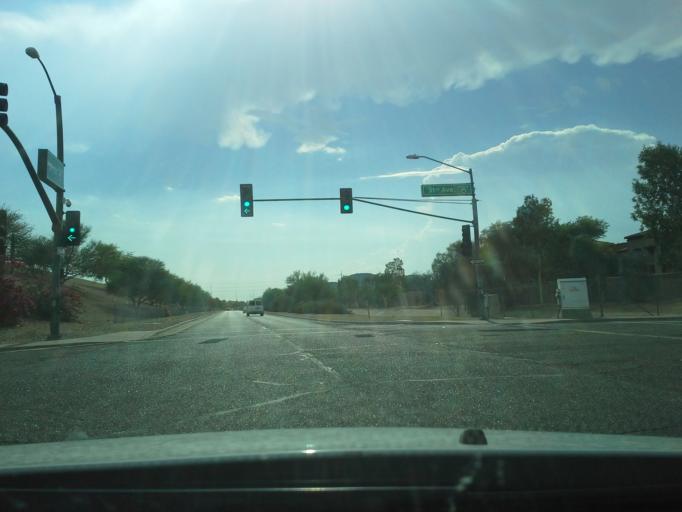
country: US
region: Arizona
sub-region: Maricopa County
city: Peoria
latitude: 33.6693
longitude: -112.1257
